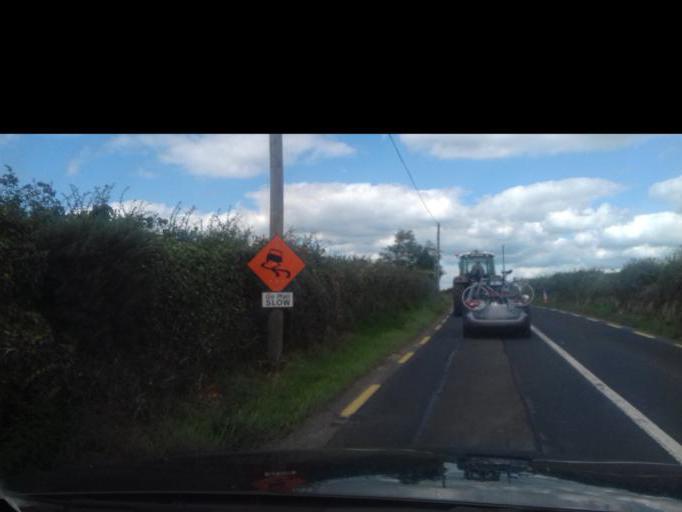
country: IE
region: Munster
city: Carrick-on-Suir
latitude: 52.2991
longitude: -7.4485
